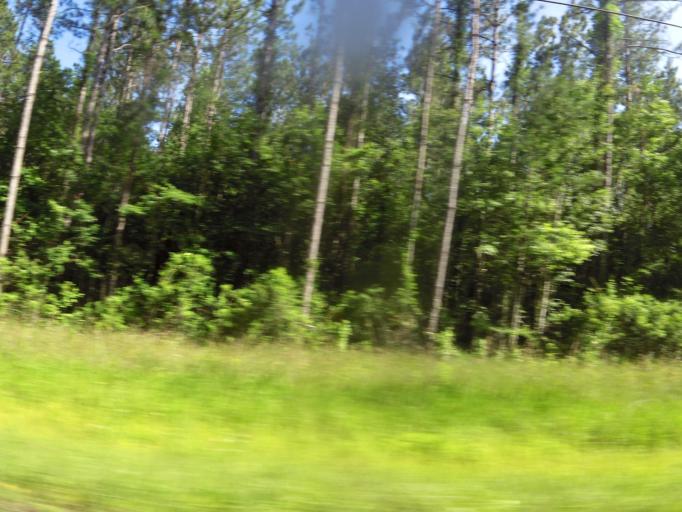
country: US
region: Florida
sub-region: Nassau County
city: Callahan
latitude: 30.5607
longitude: -81.8527
